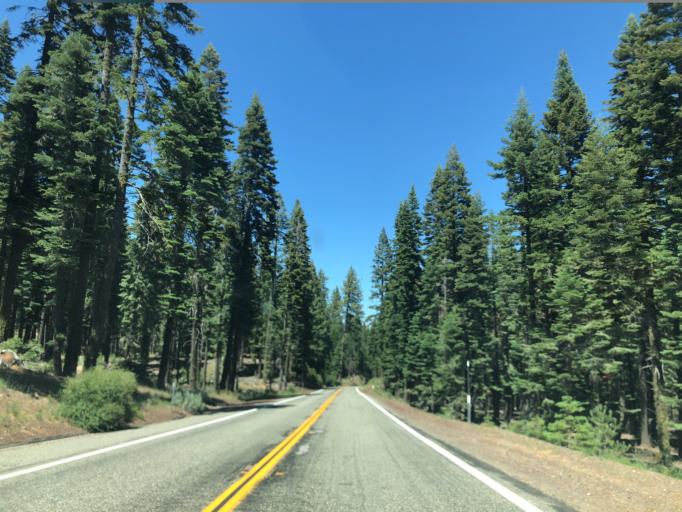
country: US
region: California
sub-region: Shasta County
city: Burney
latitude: 40.5938
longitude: -121.5362
